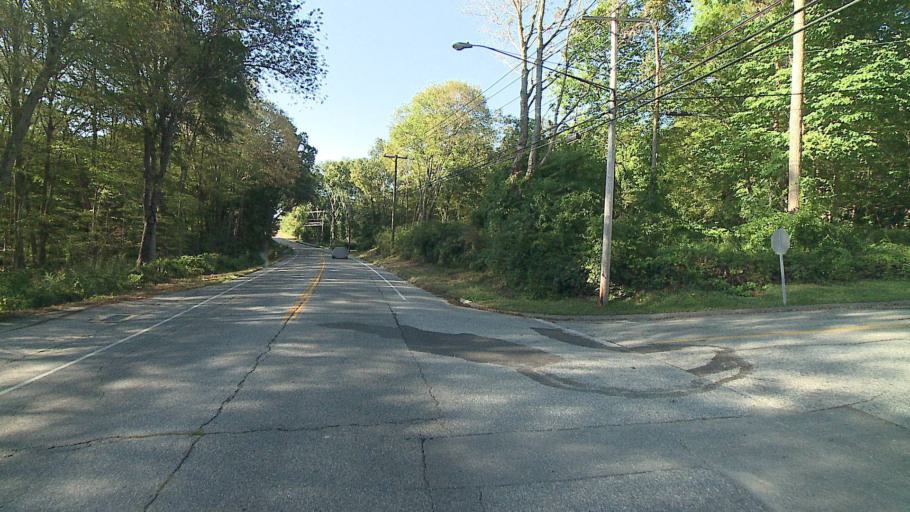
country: US
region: Connecticut
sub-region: New London County
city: Jewett City
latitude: 41.5955
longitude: -71.9915
